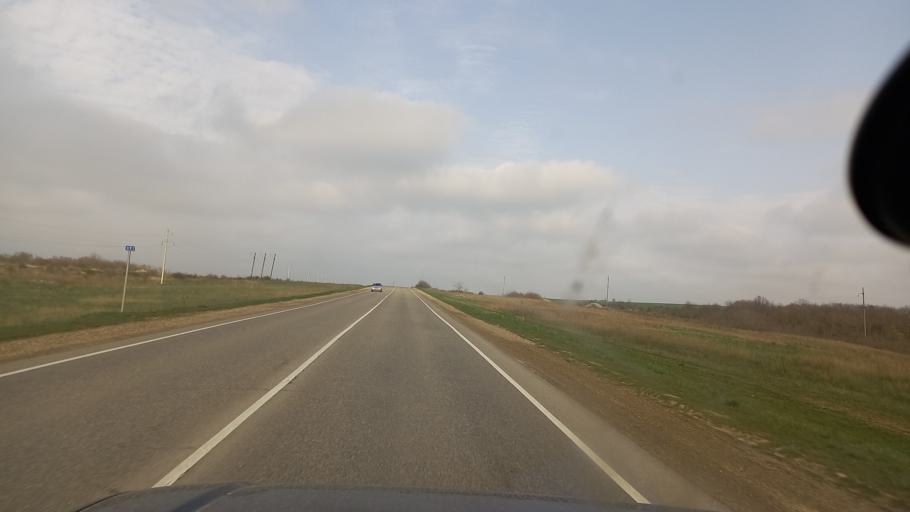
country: RU
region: Krasnodarskiy
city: Varenikovskaya
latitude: 45.0983
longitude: 37.5918
